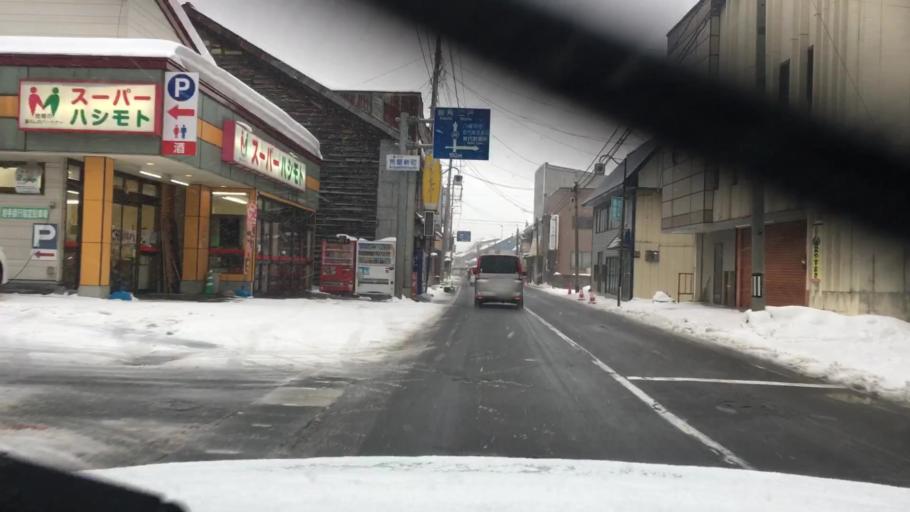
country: JP
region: Iwate
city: Ichinohe
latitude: 40.0986
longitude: 141.0478
